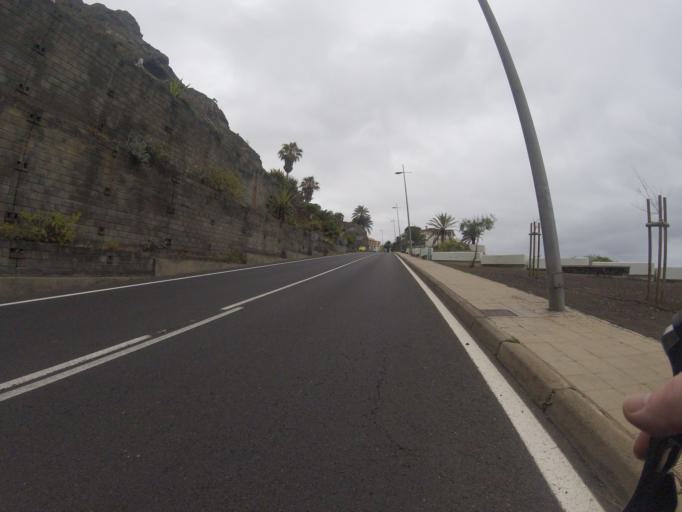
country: ES
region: Canary Islands
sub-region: Provincia de Santa Cruz de Tenerife
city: Tegueste
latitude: 28.5566
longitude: -16.3346
